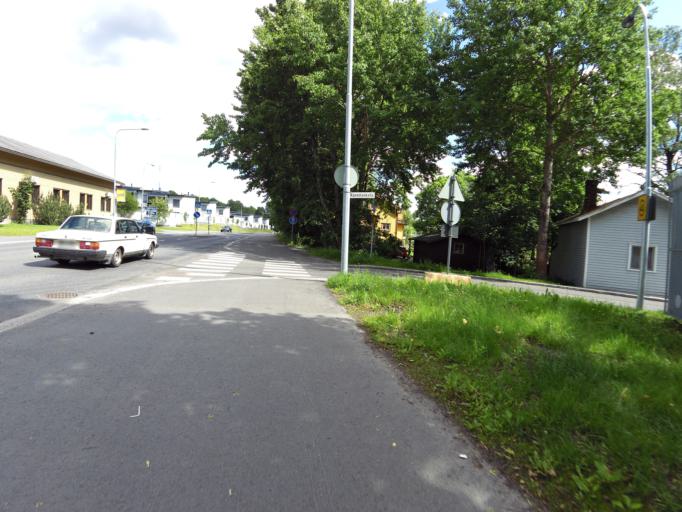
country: FI
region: Pirkanmaa
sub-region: Tampere
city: Pirkkala
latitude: 61.5086
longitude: 23.6757
